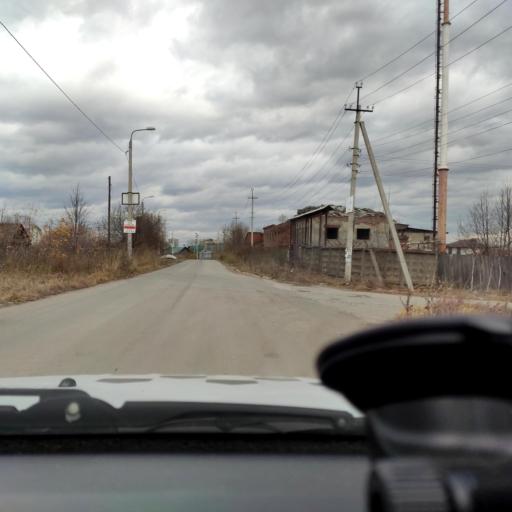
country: RU
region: Perm
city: Perm
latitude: 57.9946
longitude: 56.3376
